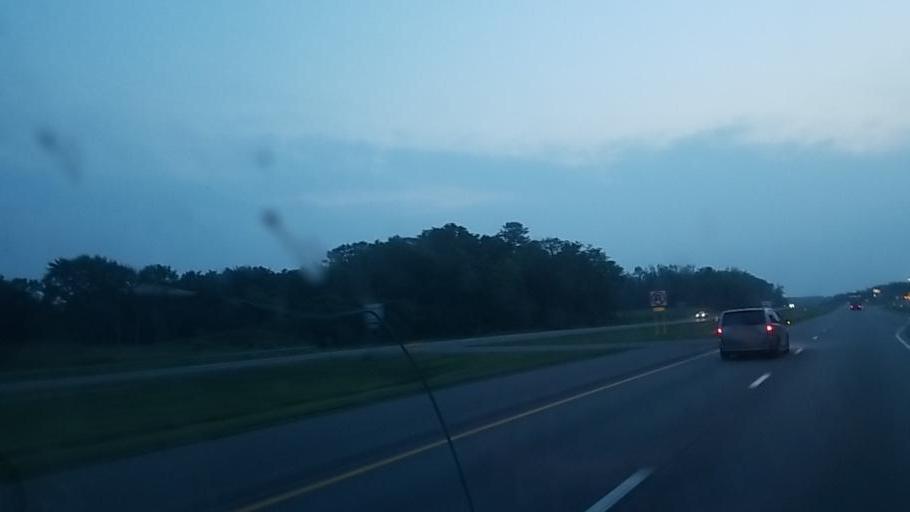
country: US
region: New York
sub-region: Madison County
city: Bolivar
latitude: 43.0948
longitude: -75.8356
